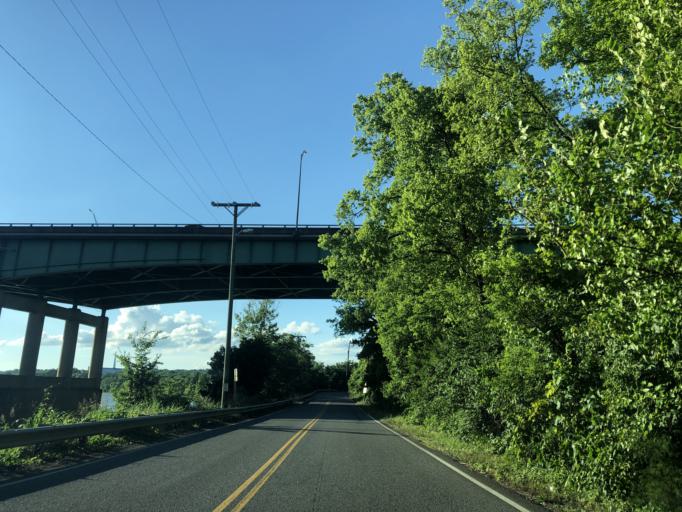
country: US
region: Tennessee
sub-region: Davidson County
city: Nashville
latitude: 36.1912
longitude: -86.7815
